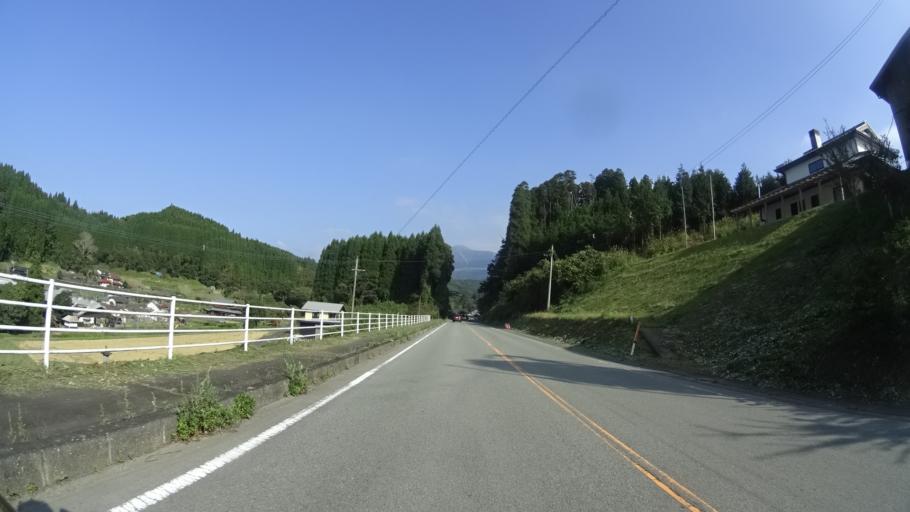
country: JP
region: Oita
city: Tsukawaki
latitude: 33.1405
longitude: 131.0953
